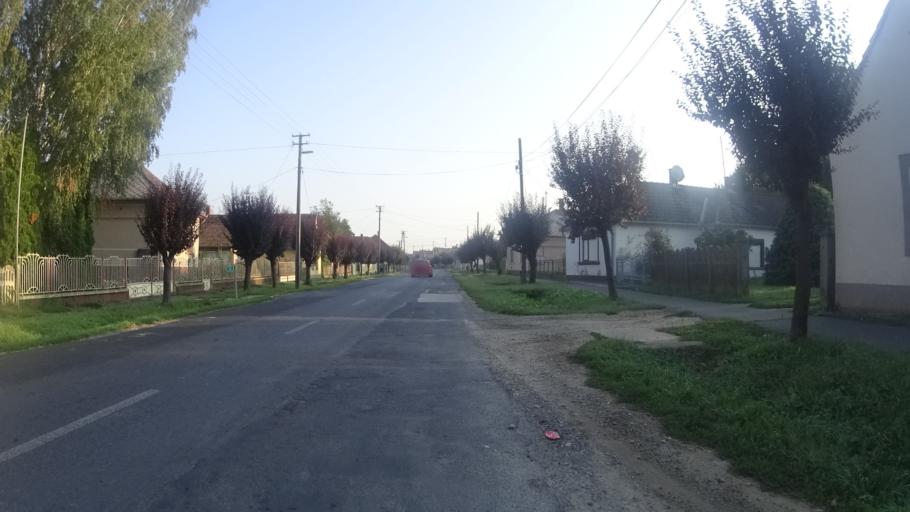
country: HU
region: Zala
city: Zalakomar
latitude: 46.5520
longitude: 17.1746
